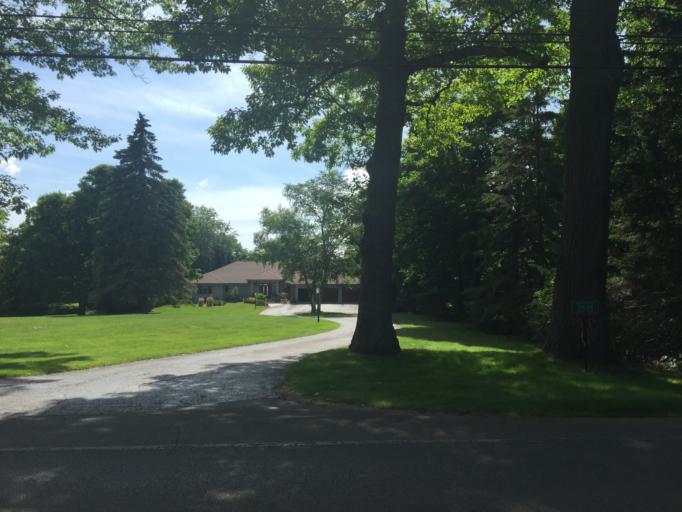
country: US
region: Wisconsin
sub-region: Door County
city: Sturgeon Bay
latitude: 44.8566
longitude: -87.3806
